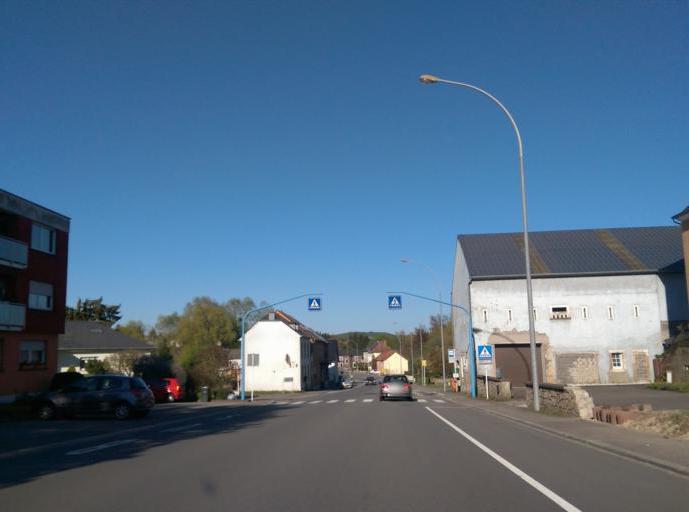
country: LU
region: Luxembourg
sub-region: Canton de Luxembourg
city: Niederanven
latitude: 49.6503
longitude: 6.2516
